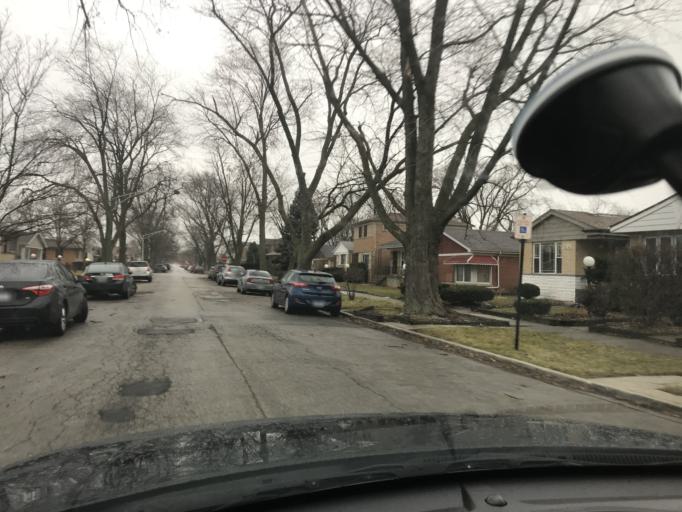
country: US
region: Illinois
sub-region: Cook County
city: Calumet Park
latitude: 41.7205
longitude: -87.6371
